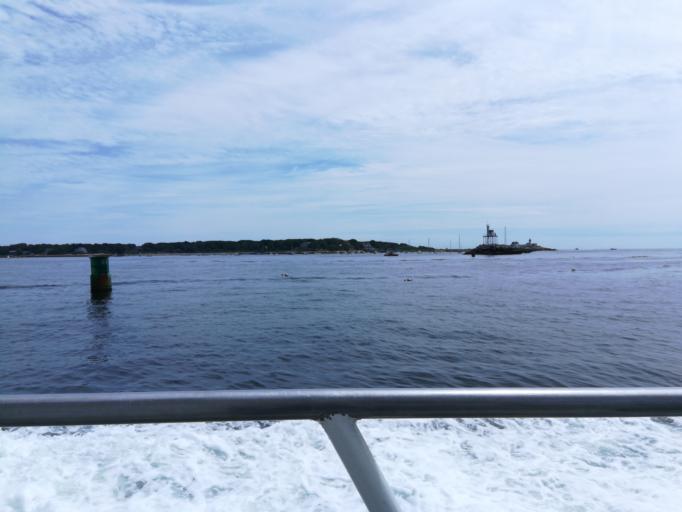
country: US
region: Massachusetts
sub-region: Essex County
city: Gloucester
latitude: 42.5834
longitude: -70.6759
